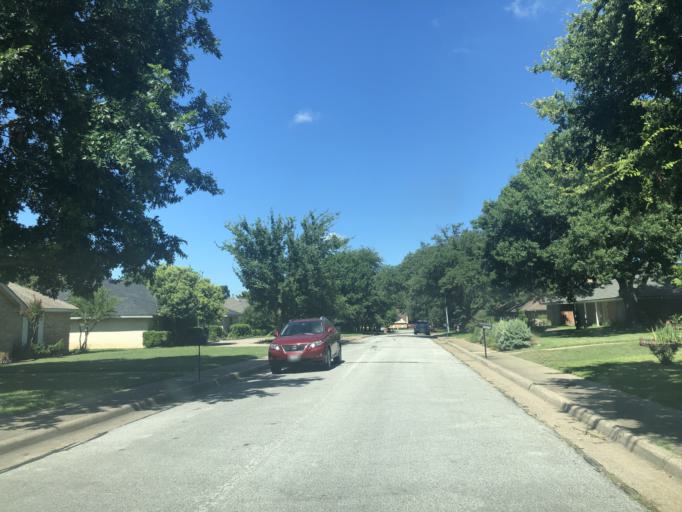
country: US
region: Texas
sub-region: Dallas County
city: Duncanville
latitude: 32.6427
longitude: -96.9355
